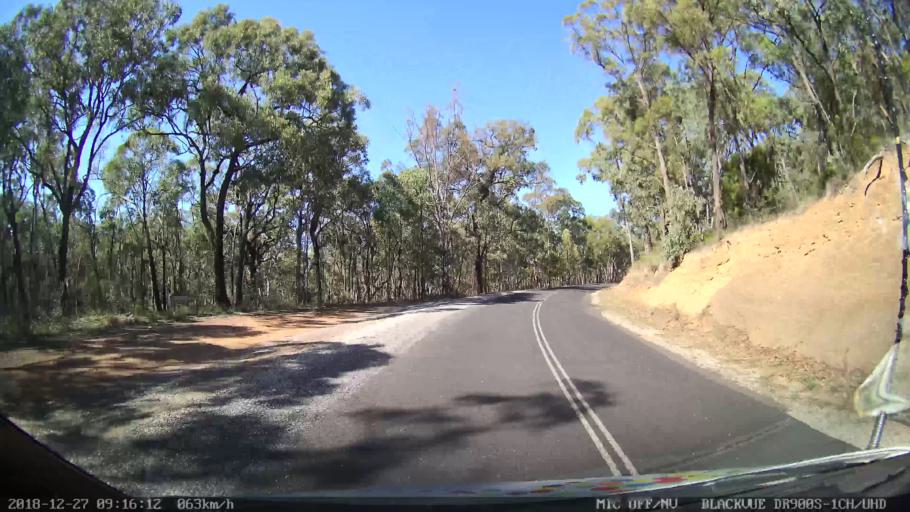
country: AU
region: New South Wales
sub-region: Lithgow
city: Portland
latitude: -33.1369
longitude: 150.0645
